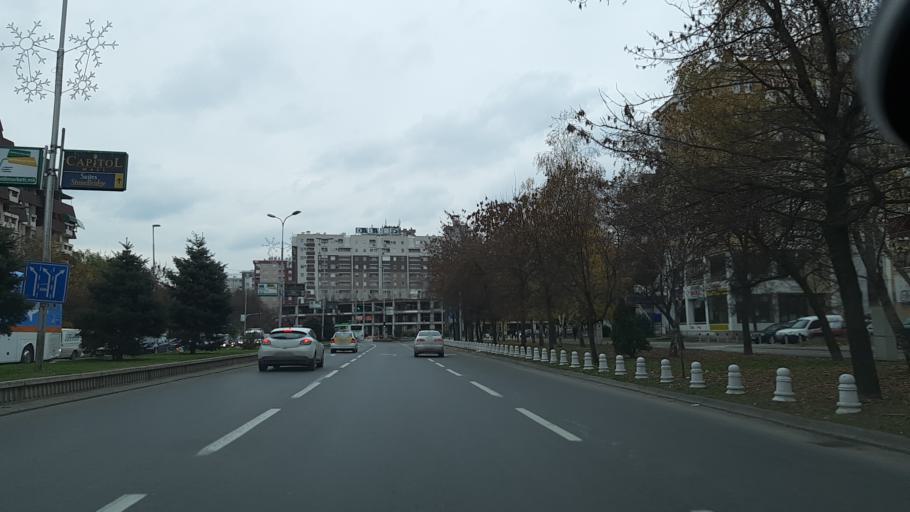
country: MK
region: Karpos
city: Skopje
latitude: 41.9885
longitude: 21.4503
